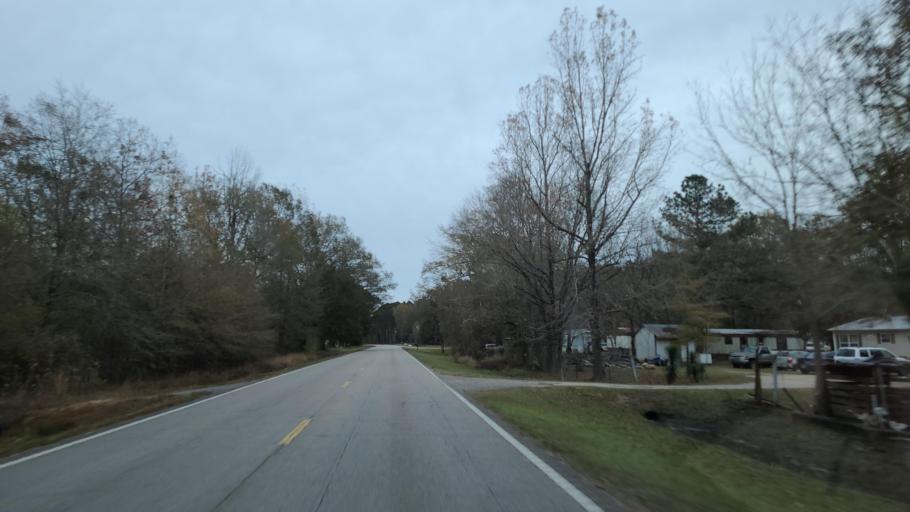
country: US
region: Mississippi
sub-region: Clarke County
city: Stonewall
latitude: 32.0296
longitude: -88.8651
